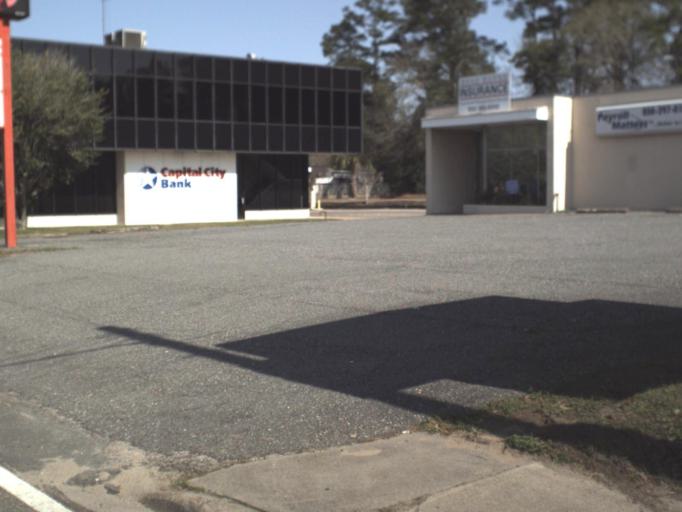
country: US
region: Florida
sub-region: Leon County
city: Tallahassee
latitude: 30.4687
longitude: -84.2866
